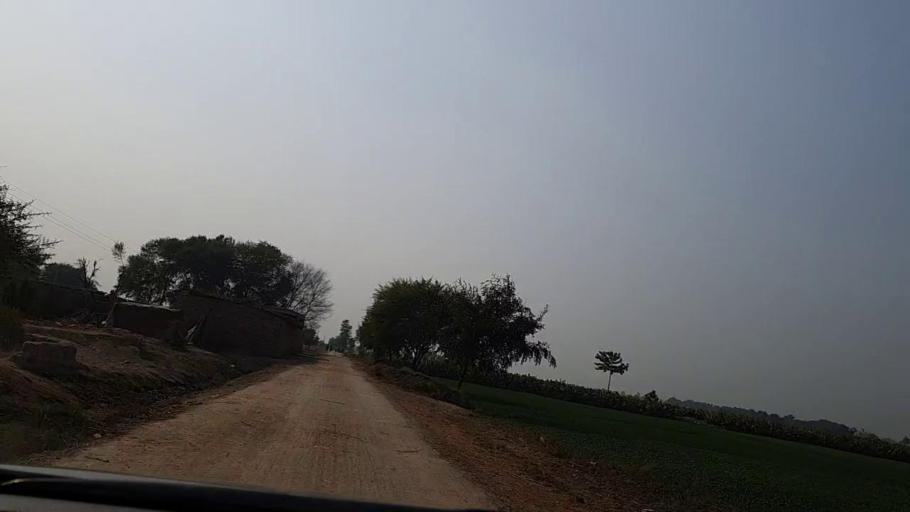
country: PK
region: Sindh
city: Sakrand
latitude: 26.1488
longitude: 68.2413
